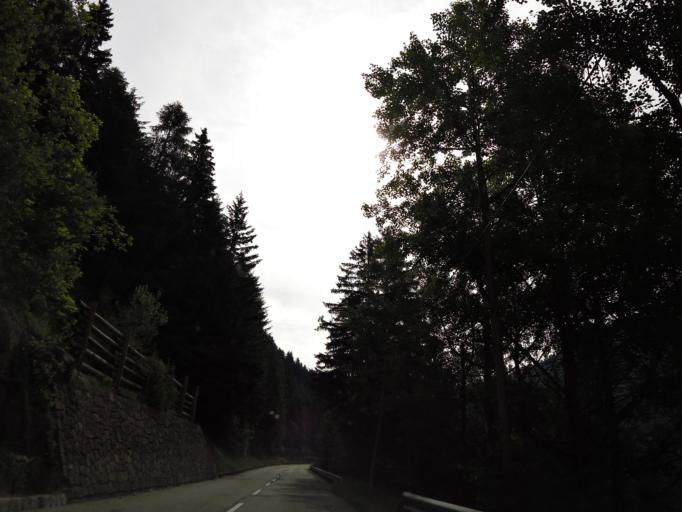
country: IT
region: Trentino-Alto Adige
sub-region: Bolzano
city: Siusi
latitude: 46.5399
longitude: 11.5913
